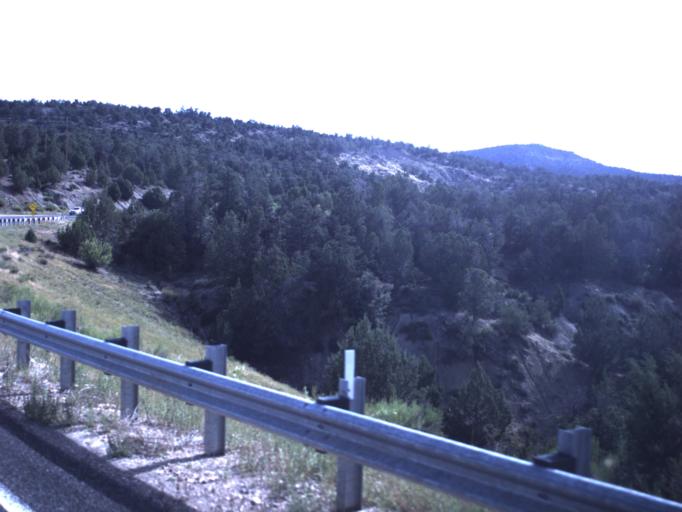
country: US
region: Utah
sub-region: Washington County
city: Hildale
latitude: 37.2606
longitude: -112.7914
